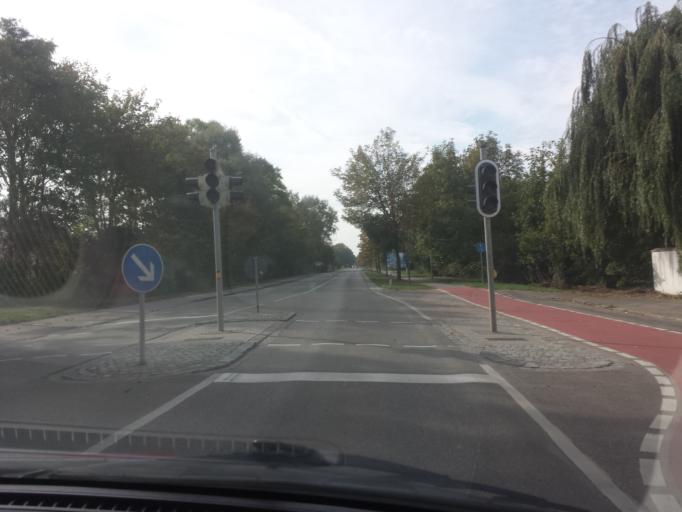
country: DE
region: Bavaria
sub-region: Upper Bavaria
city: Bergheim
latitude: 48.7373
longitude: 11.2280
